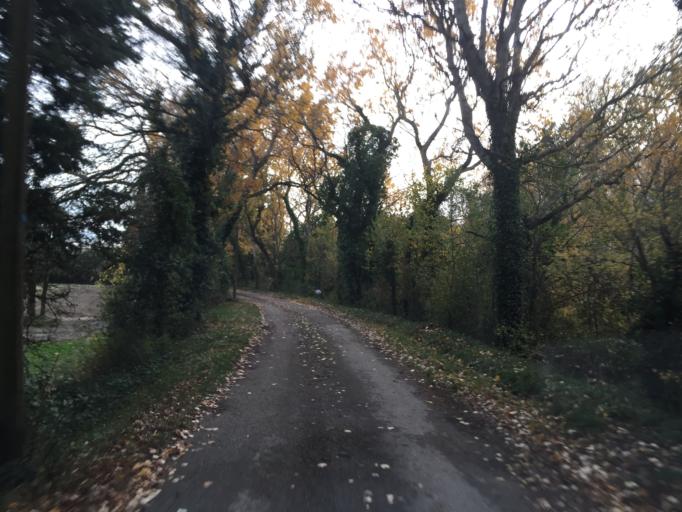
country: FR
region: Provence-Alpes-Cote d'Azur
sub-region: Departement du Vaucluse
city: Sarrians
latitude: 44.0681
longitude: 4.9321
